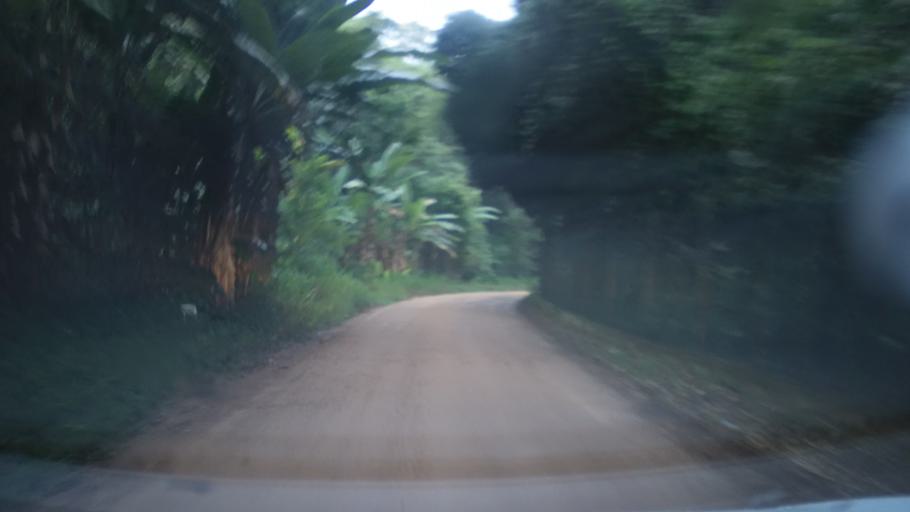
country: BR
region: Sao Paulo
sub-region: Itupeva
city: Itupeva
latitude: -23.1660
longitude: -47.0684
